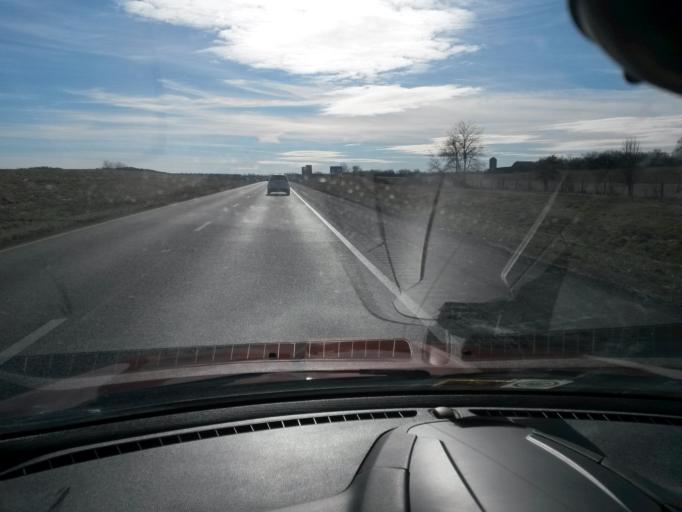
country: US
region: Virginia
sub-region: Rockingham County
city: Dayton
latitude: 38.3767
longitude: -78.9187
